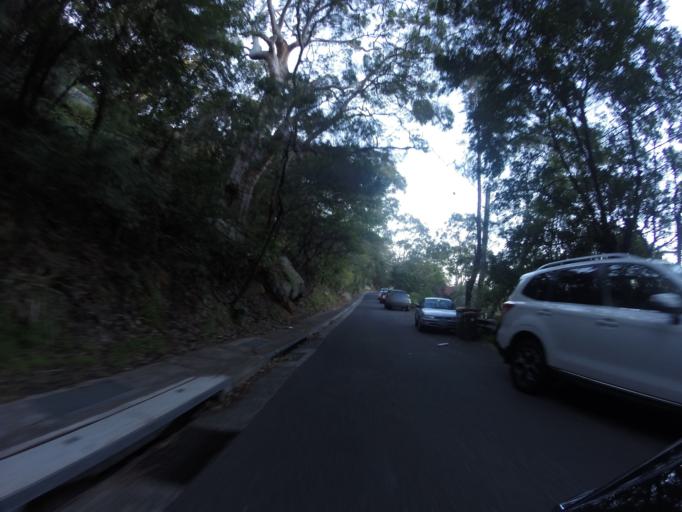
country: AU
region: New South Wales
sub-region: Sutherland Shire
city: Grays Point
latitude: -34.0607
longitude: 151.0840
